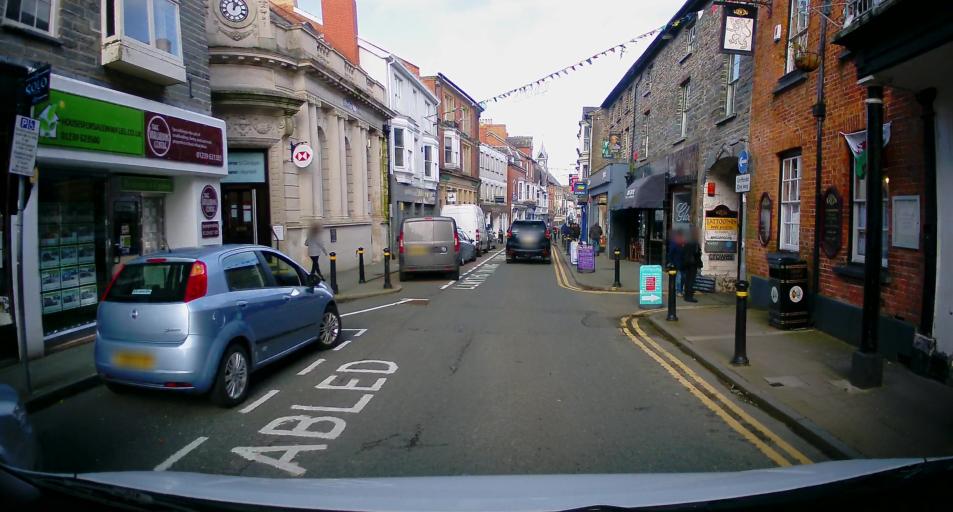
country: GB
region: Wales
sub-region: County of Ceredigion
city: Cardigan
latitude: 52.0826
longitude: -4.6613
